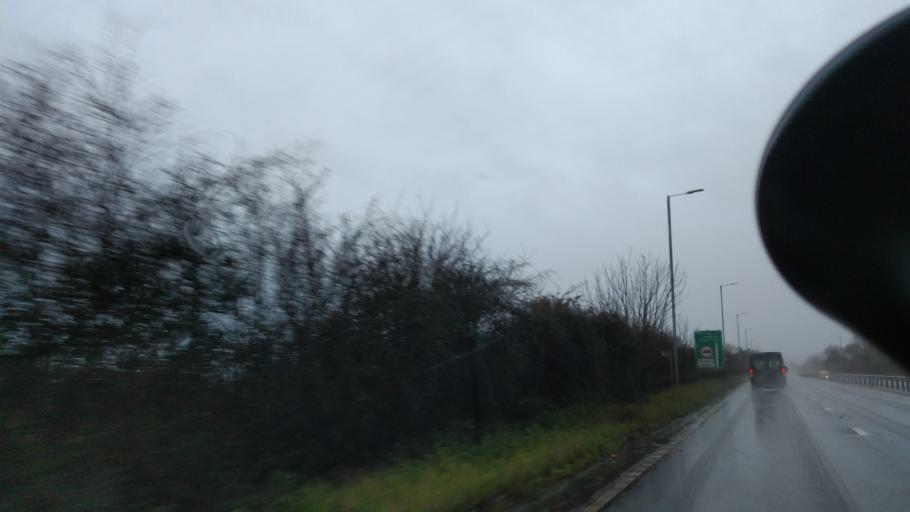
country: GB
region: England
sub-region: West Sussex
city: Lancing
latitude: 50.8373
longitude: -0.3466
